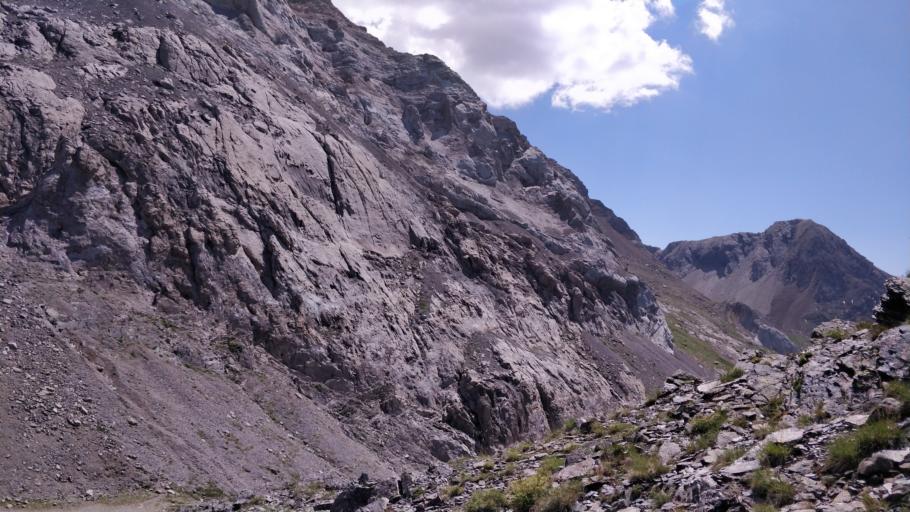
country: ES
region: Aragon
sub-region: Provincia de Huesca
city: Broto
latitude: 42.7048
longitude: -0.0643
